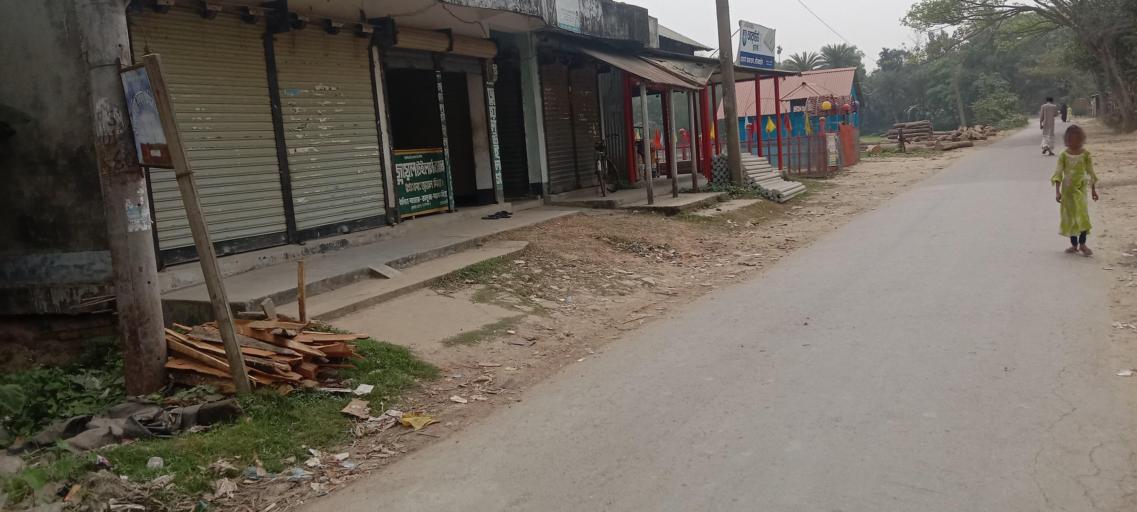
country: BD
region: Dhaka
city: Gafargaon
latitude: 24.4608
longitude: 90.4107
